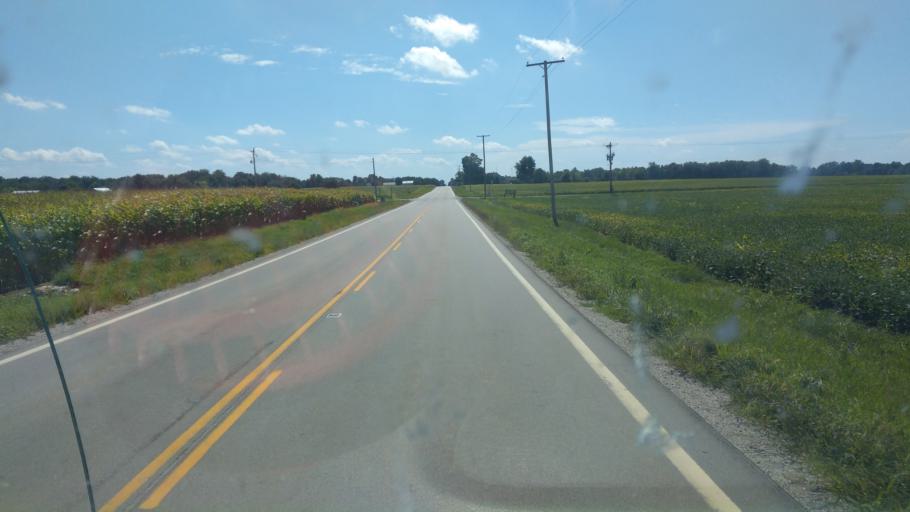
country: US
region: Ohio
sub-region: Wyandot County
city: Upper Sandusky
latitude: 40.7906
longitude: -83.1308
